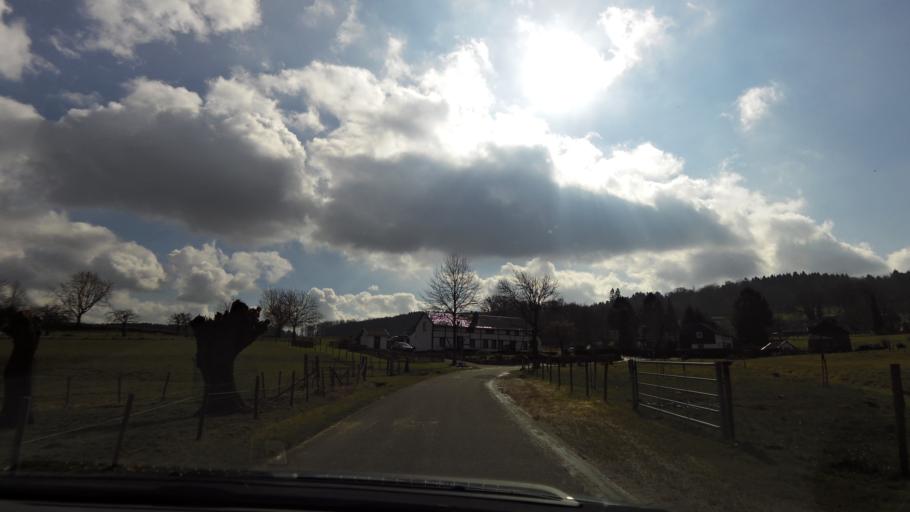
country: NL
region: Limburg
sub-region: Gemeente Vaals
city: Vaals
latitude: 50.7618
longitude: 5.9883
